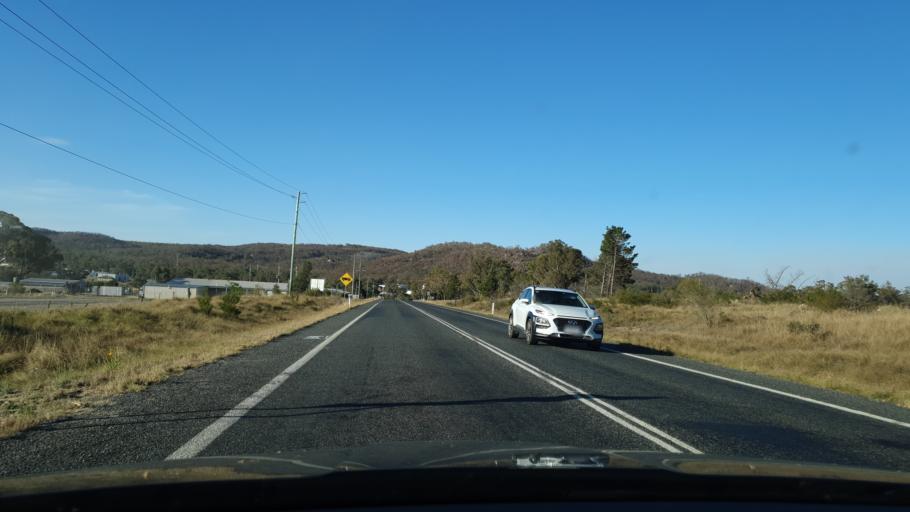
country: AU
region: Queensland
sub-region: Southern Downs
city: Stanthorpe
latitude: -28.6588
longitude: 151.9168
